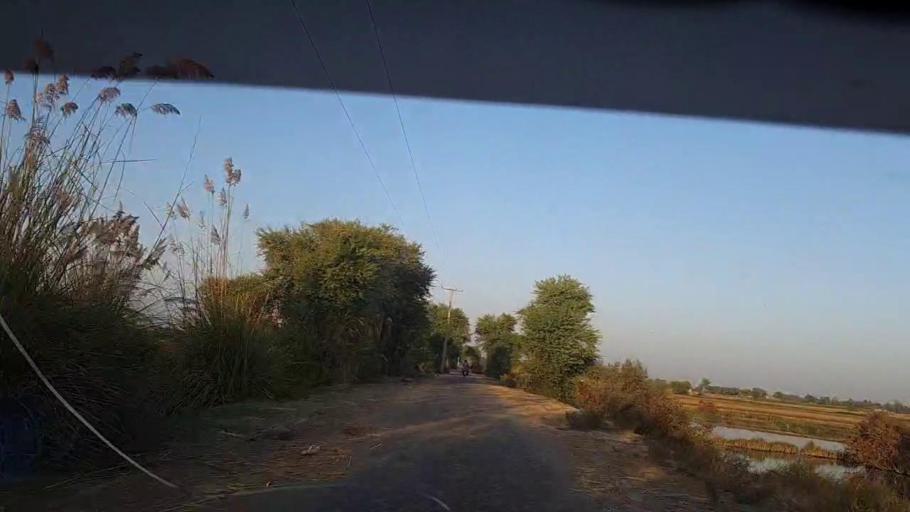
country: PK
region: Sindh
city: Ratodero
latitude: 27.8989
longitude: 68.2312
